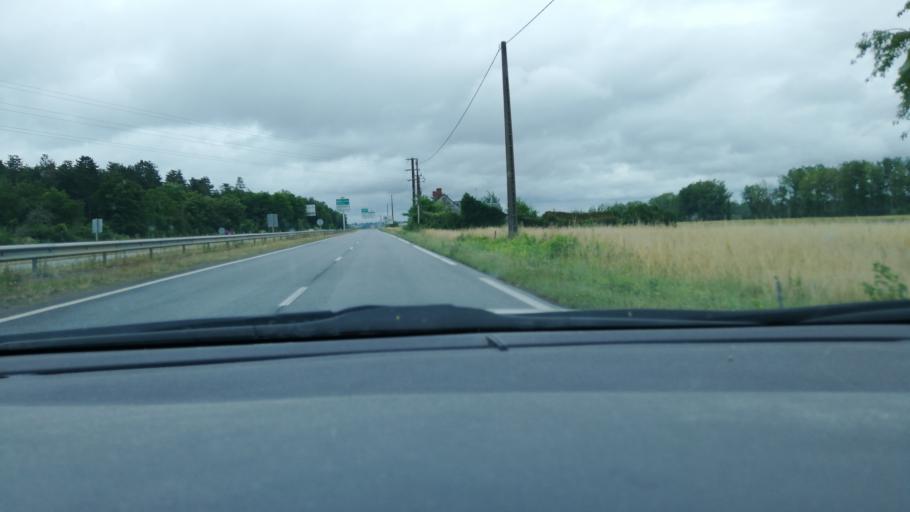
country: FR
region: Poitou-Charentes
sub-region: Departement de la Vienne
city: Cenon-sur-Vienne
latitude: 46.7752
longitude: 0.5141
